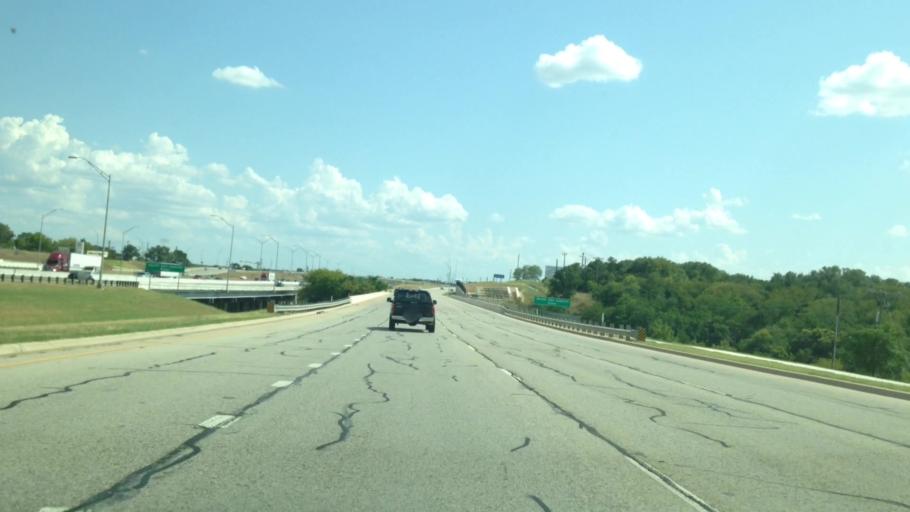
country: US
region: Texas
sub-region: Williamson County
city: Georgetown
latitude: 30.6277
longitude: -97.6923
